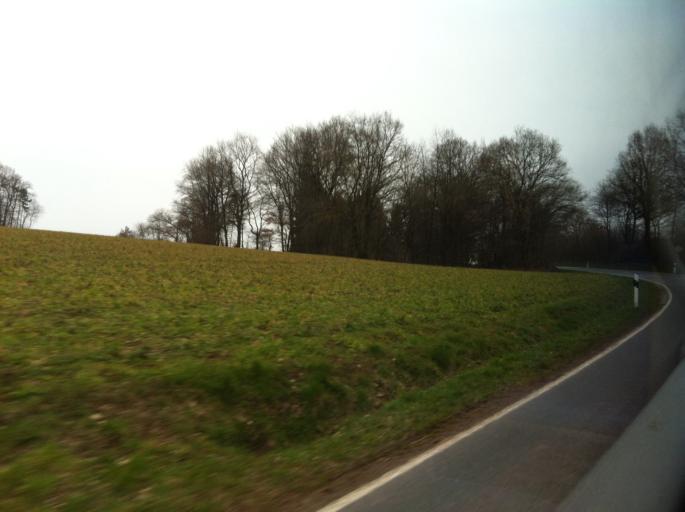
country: DE
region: Baden-Wuerttemberg
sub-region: Karlsruhe Region
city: Fahrenbach
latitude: 49.4061
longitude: 9.1482
